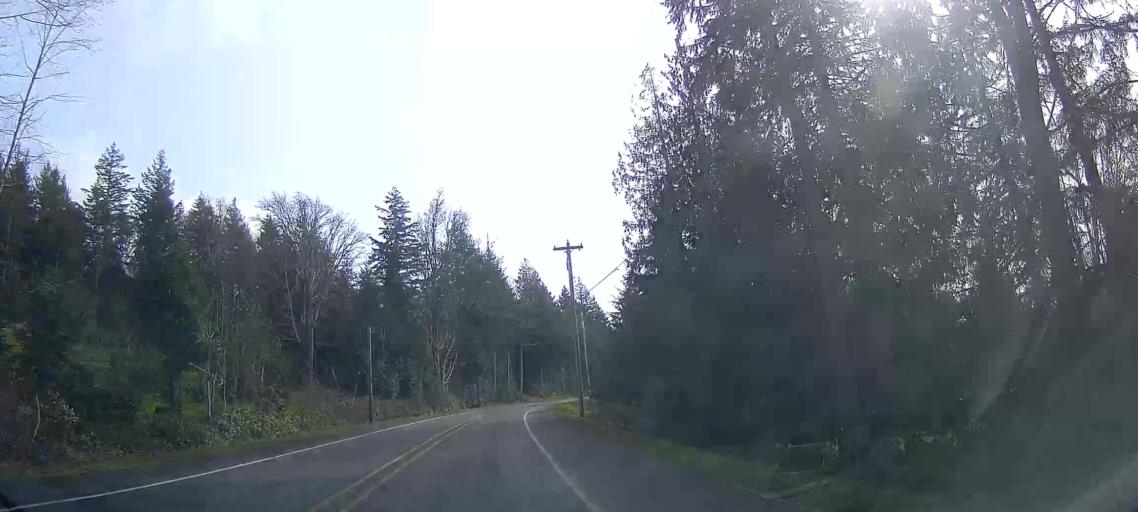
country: US
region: Washington
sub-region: Island County
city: Camano
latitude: 48.1353
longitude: -122.4653
